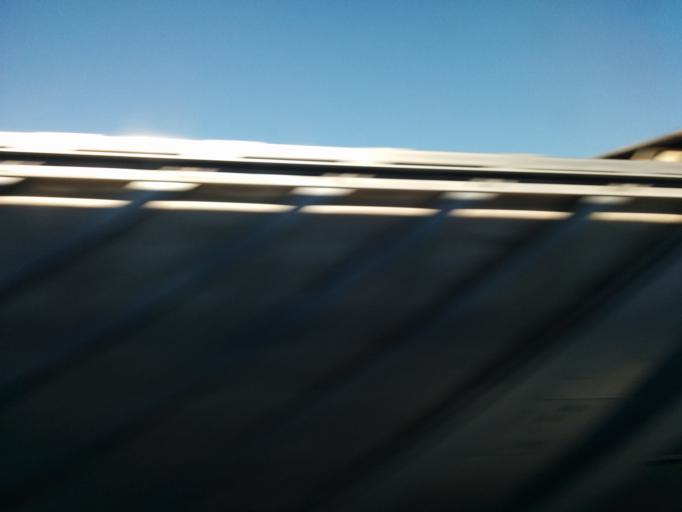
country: JP
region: Kanagawa
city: Isehara
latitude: 35.3574
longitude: 139.3227
